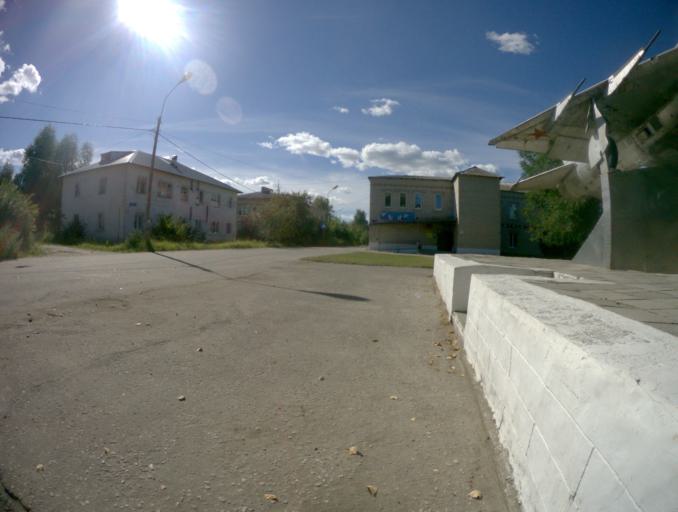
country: RU
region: Vladimir
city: Krasnaya Gorbatka
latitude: 55.8673
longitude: 41.7601
